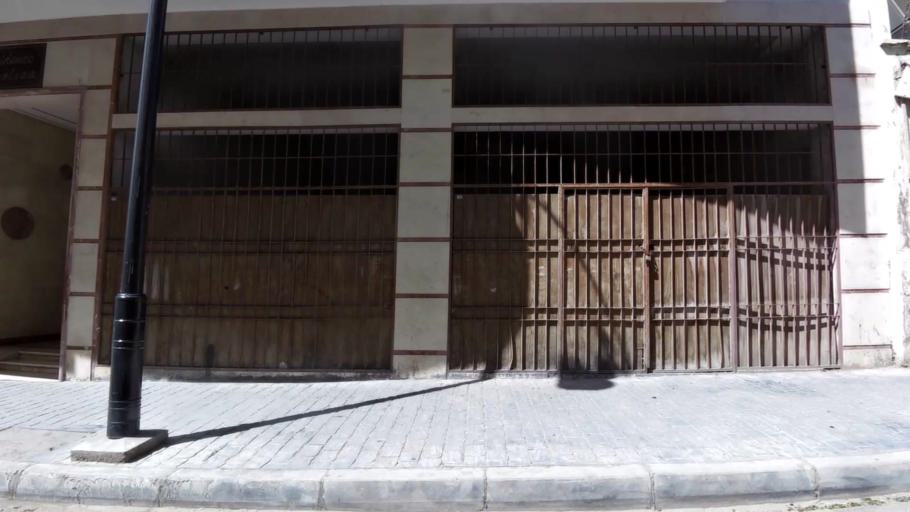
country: MA
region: Tanger-Tetouan
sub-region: Tanger-Assilah
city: Tangier
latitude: 35.7868
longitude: -5.8206
